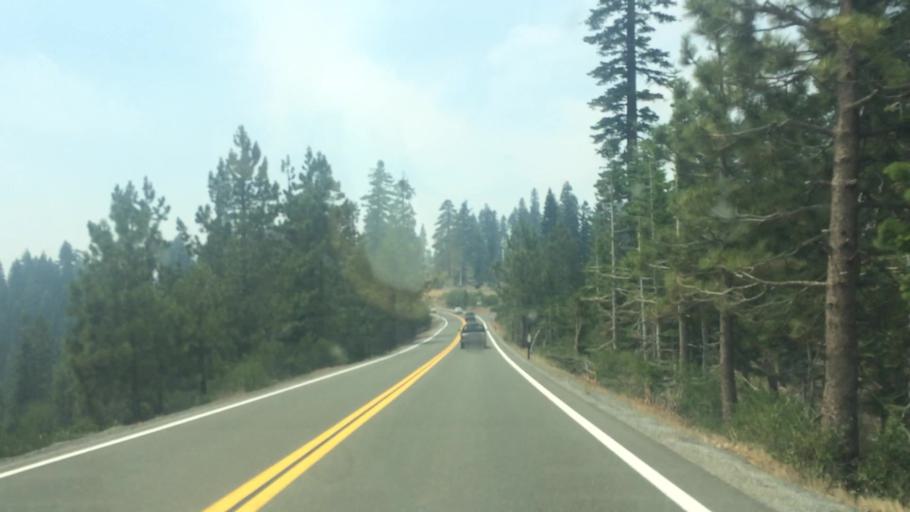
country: US
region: California
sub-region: Calaveras County
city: Arnold
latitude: 38.5849
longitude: -120.2481
